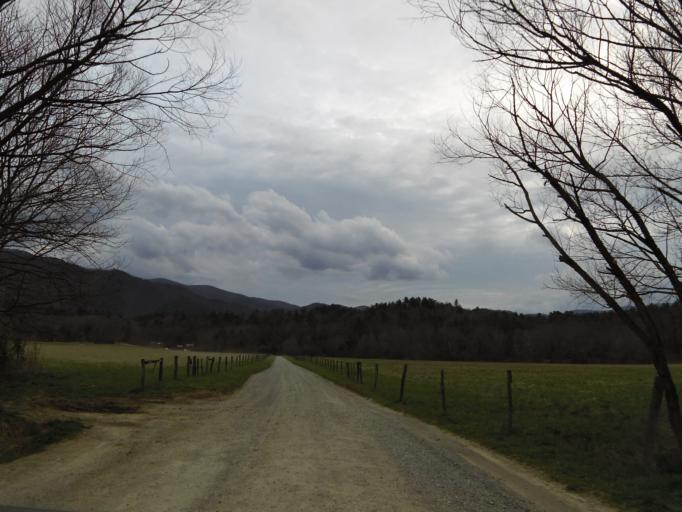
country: US
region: Tennessee
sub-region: Blount County
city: Wildwood
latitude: 35.5923
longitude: -83.8239
